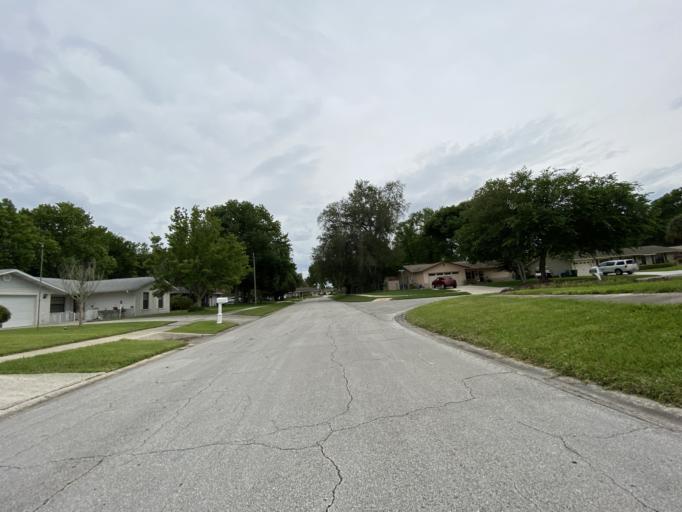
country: US
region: Florida
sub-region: Volusia County
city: South Daytona
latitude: 29.1727
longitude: -81.0146
